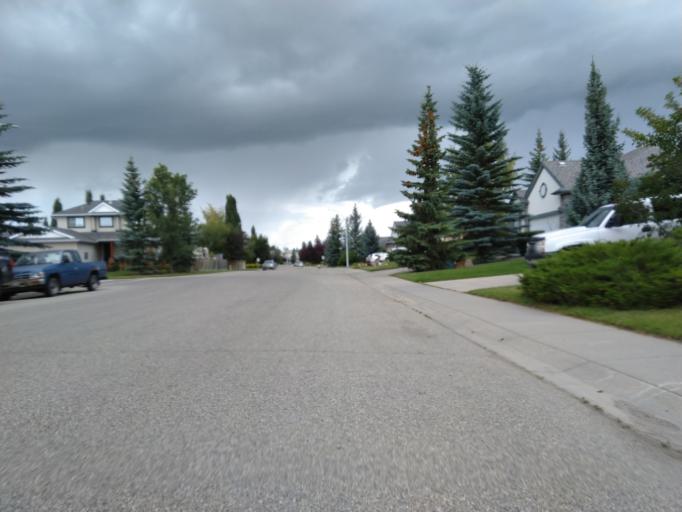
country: CA
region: Alberta
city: Cochrane
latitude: 51.1857
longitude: -114.4944
